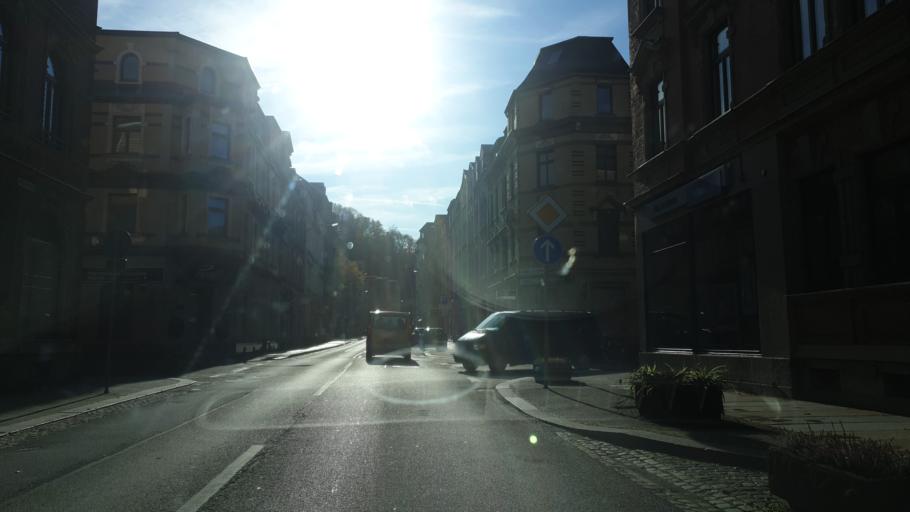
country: DE
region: Saxony
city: Aue
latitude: 50.5843
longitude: 12.7003
